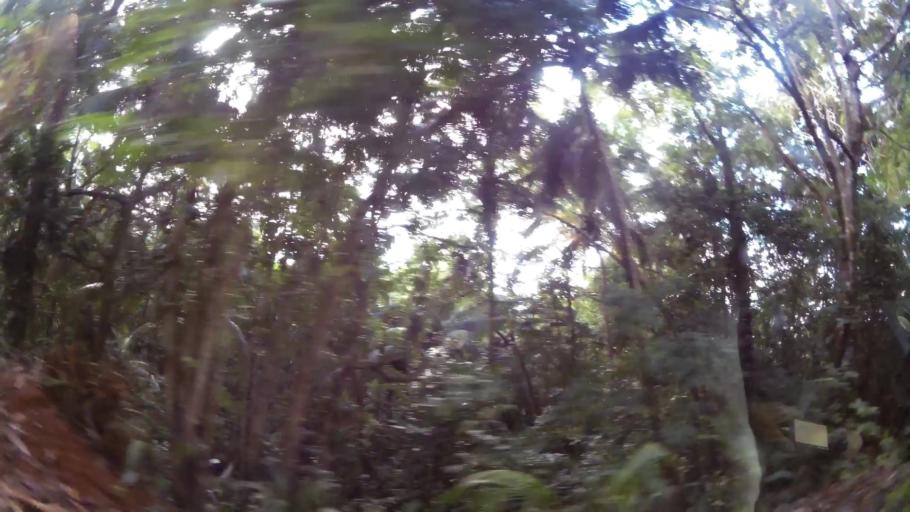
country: DM
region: Saint Andrew
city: Calibishie
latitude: 15.5933
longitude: -61.3753
